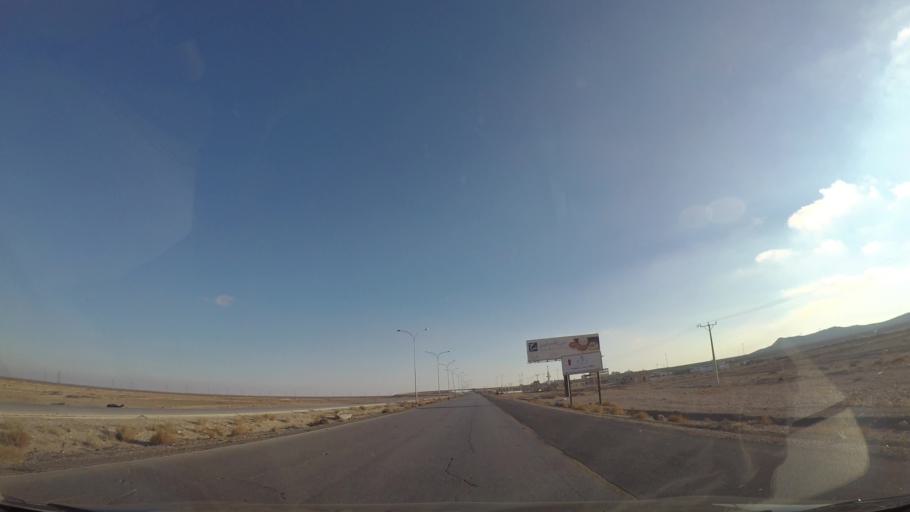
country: JO
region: Tafielah
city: Busayra
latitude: 30.5096
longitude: 35.7997
